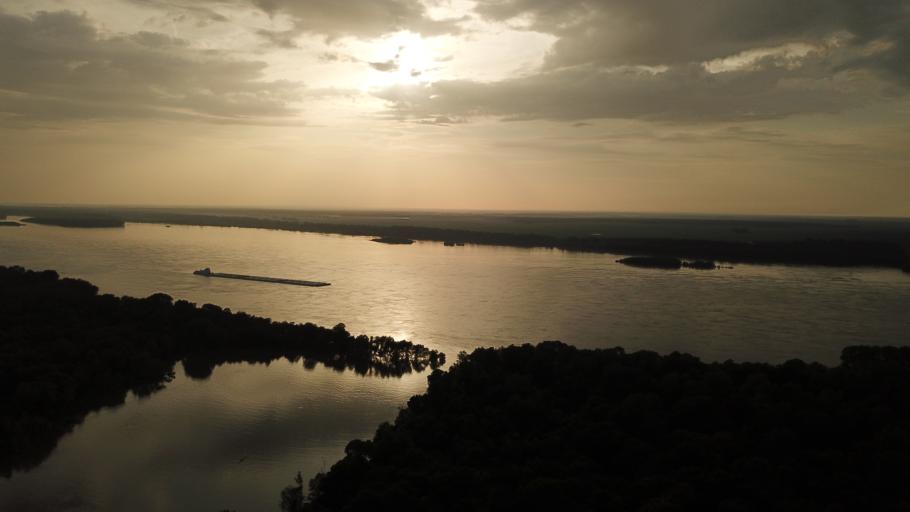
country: US
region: Mississippi
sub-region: Tunica County
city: North Tunica
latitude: 34.8498
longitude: -90.3325
